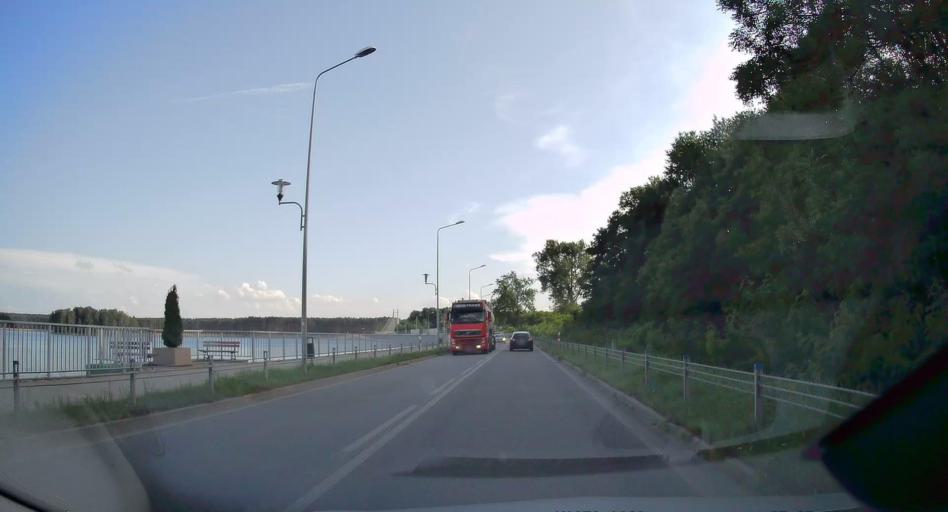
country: PL
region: Swietokrzyskie
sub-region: Powiat konecki
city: Smykow
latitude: 51.1159
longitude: 20.3504
